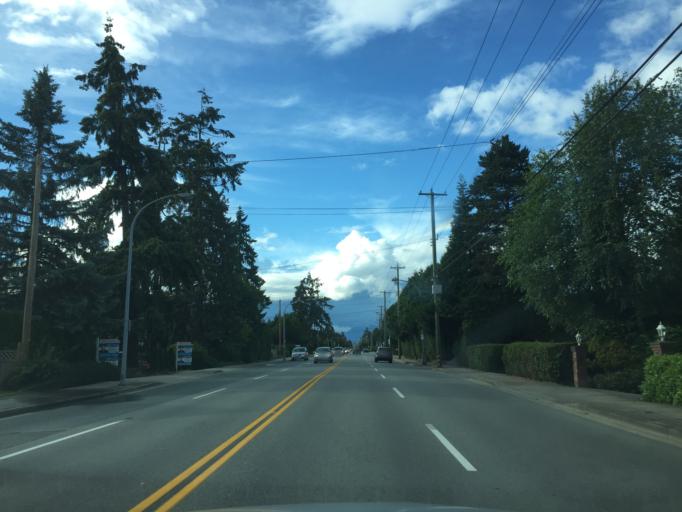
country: CA
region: British Columbia
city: Richmond
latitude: 49.1527
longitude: -123.1141
